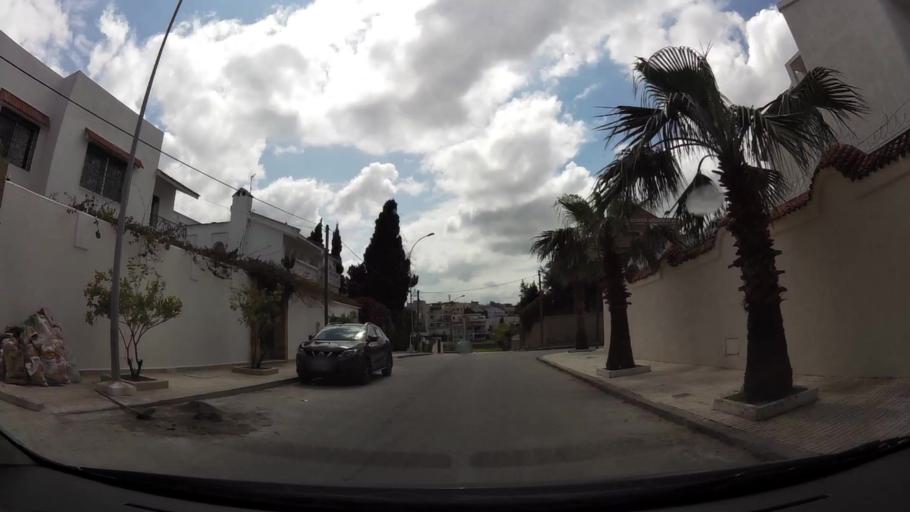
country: MA
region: Tanger-Tetouan
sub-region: Tanger-Assilah
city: Tangier
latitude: 35.7739
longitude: -5.7729
